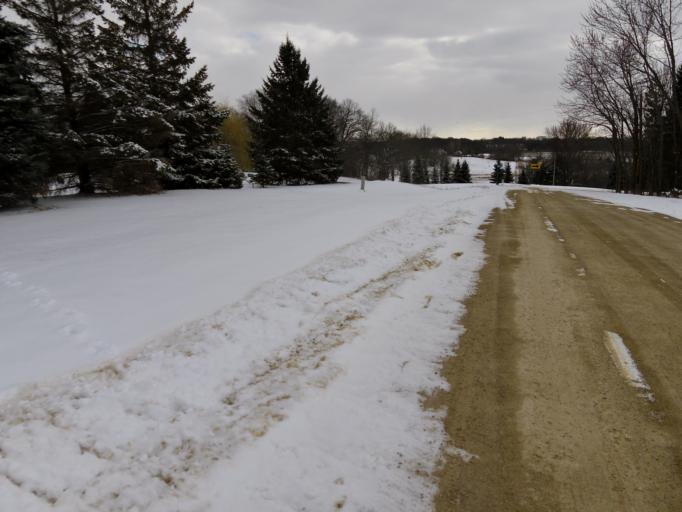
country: US
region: Minnesota
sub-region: Scott County
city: Prior Lake
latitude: 44.6840
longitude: -93.4526
